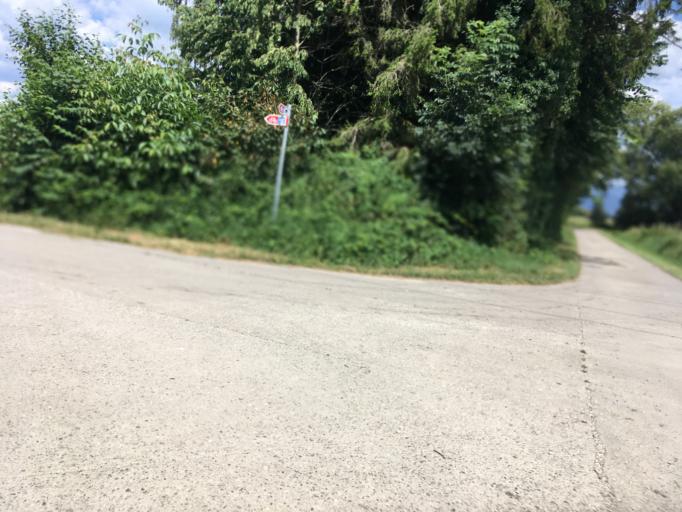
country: CH
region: Fribourg
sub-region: See District
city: Bas-Vully
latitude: 46.9674
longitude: 7.0694
